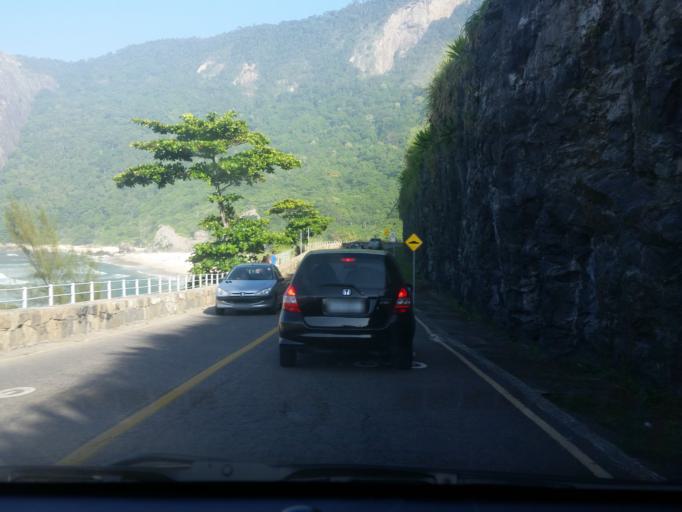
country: BR
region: Rio de Janeiro
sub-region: Nilopolis
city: Nilopolis
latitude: -23.0400
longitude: -43.5014
